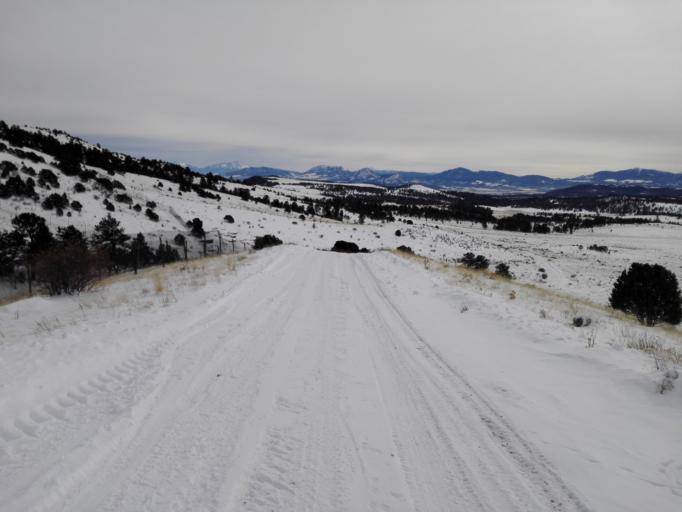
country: US
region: Colorado
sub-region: Custer County
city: Westcliffe
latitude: 37.9623
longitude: -105.2154
